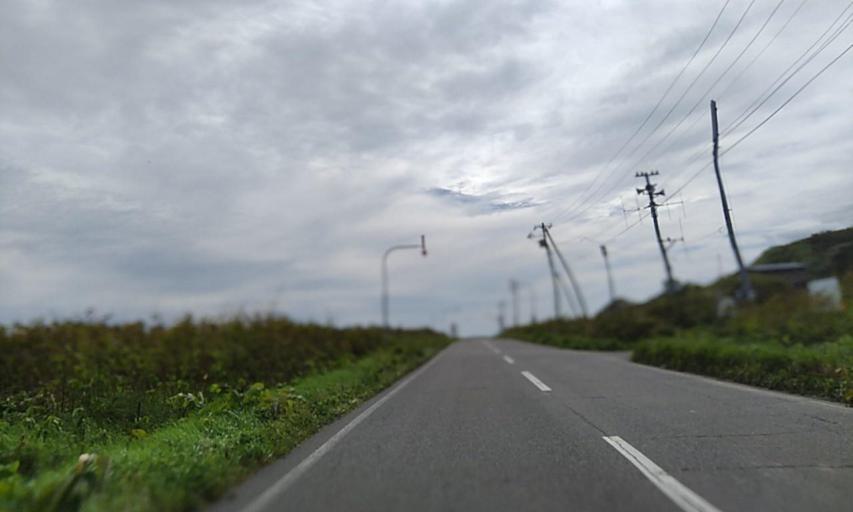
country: JP
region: Hokkaido
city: Obihiro
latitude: 42.7847
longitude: 143.7878
